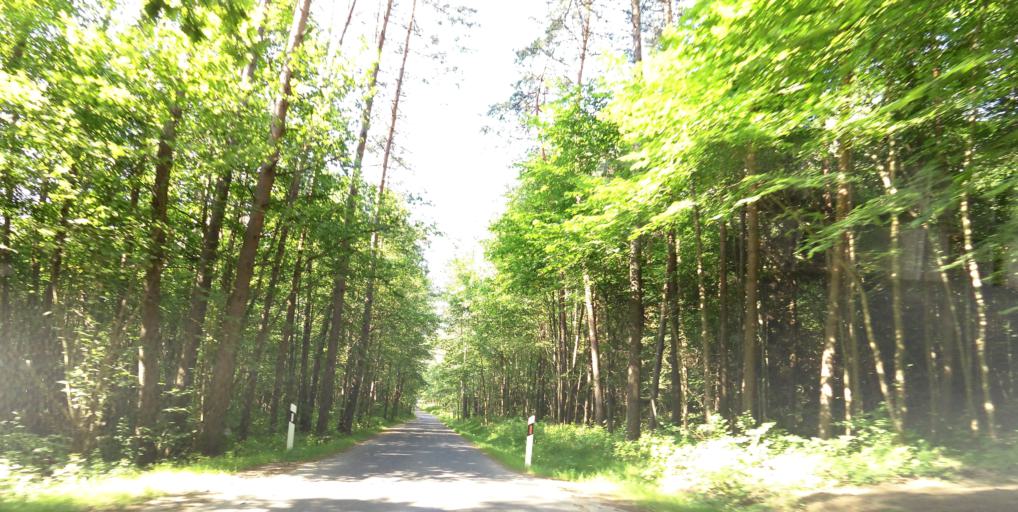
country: LT
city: Grigiskes
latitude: 54.7265
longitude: 25.0625
